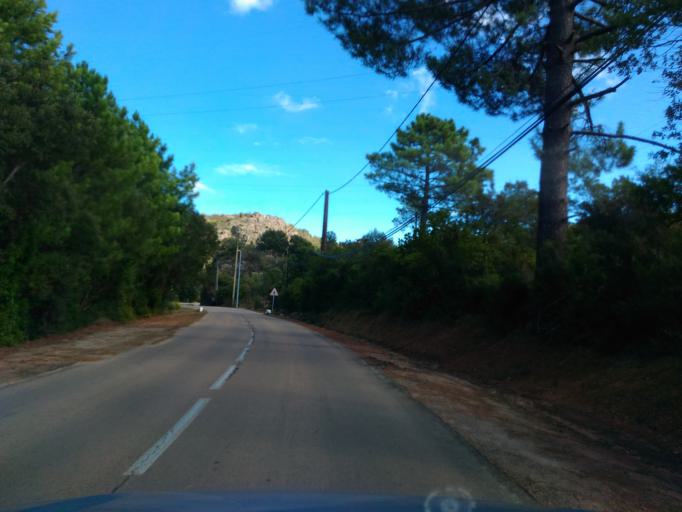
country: FR
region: Corsica
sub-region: Departement de la Corse-du-Sud
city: Porto-Vecchio
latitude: 41.7061
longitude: 9.3314
